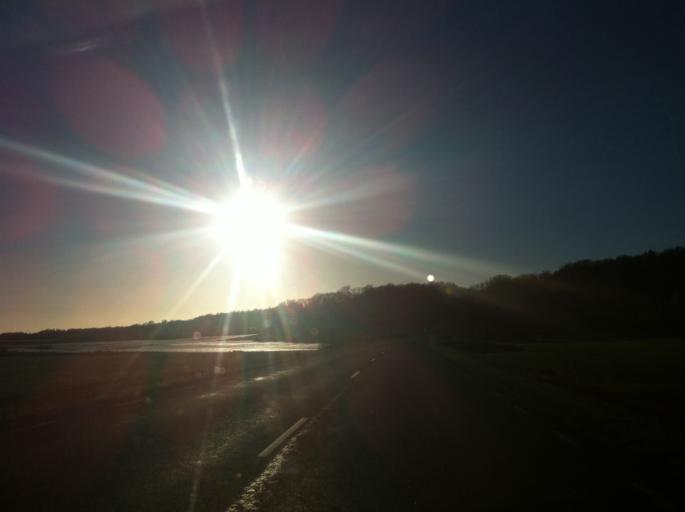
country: SE
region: Skane
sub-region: Bromolla Kommun
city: Nasum
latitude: 56.1795
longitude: 14.5090
